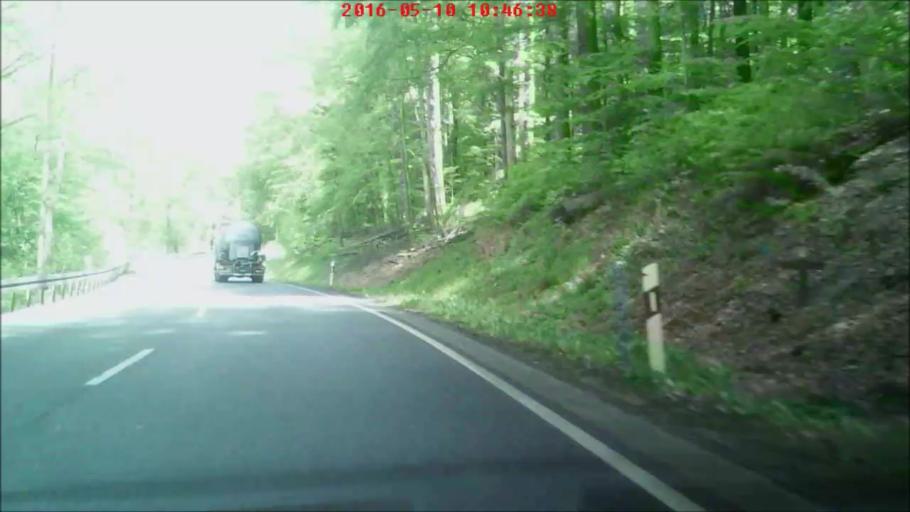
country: DE
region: Hesse
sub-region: Regierungsbezirk Kassel
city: Burghaun
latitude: 50.7434
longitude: 9.6885
